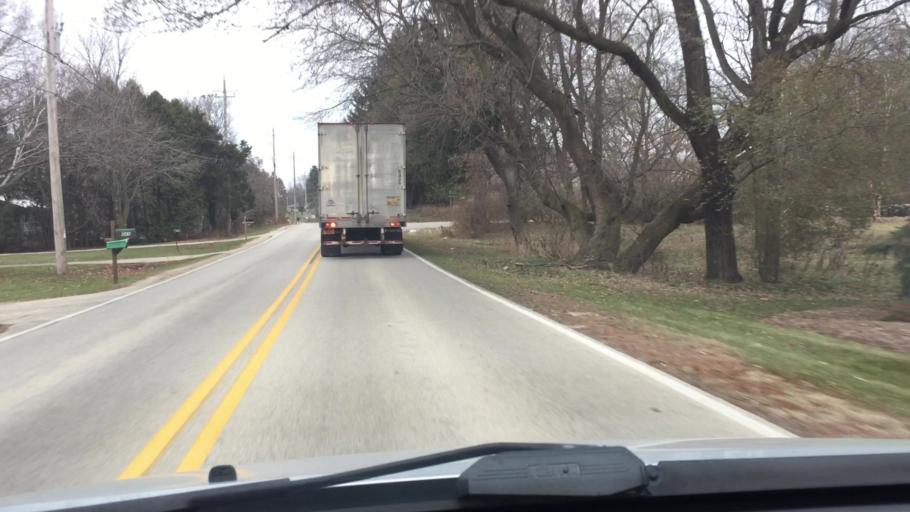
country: US
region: Wisconsin
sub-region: Ozaukee County
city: Cedarburg
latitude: 43.2928
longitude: -87.9630
